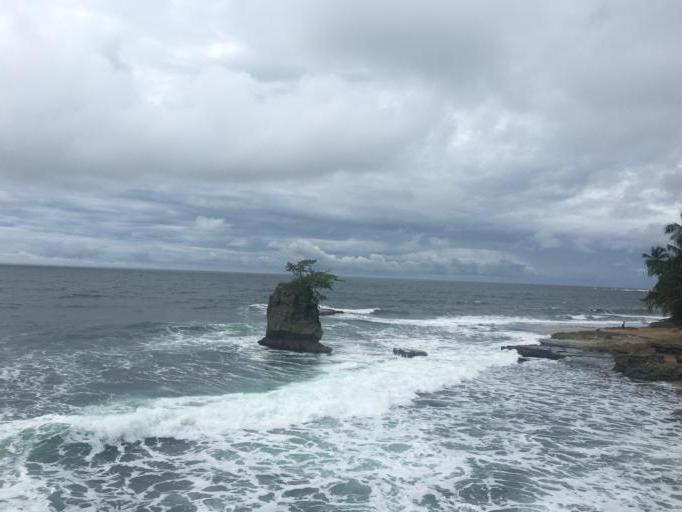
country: CR
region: Limon
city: Sixaola
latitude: 9.6399
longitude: -82.6492
